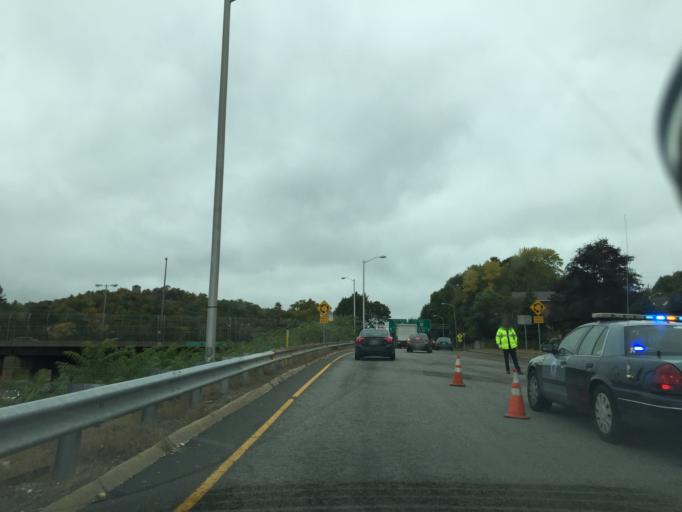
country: US
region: Massachusetts
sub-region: Middlesex County
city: Medford
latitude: 42.4278
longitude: -71.1028
